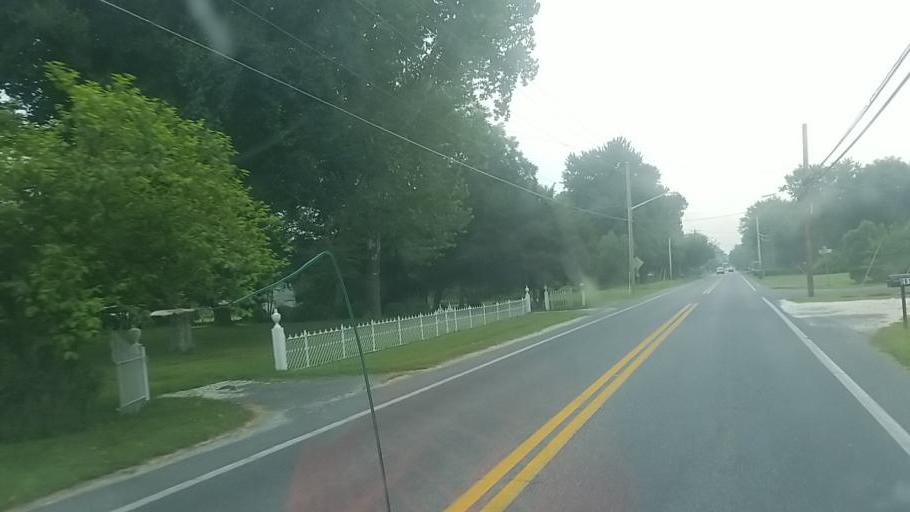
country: US
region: Maryland
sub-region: Wicomico County
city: Salisbury
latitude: 38.3732
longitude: -75.5476
